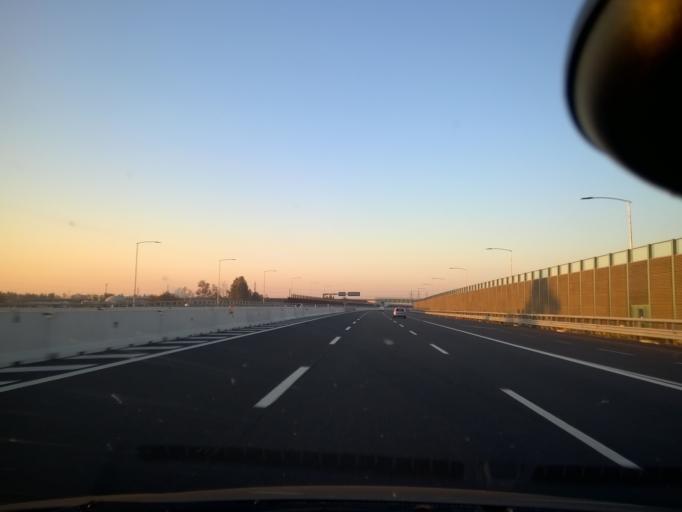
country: IT
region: Lombardy
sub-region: Citta metropolitana di Milano
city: Liscate
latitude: 45.4703
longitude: 9.4318
